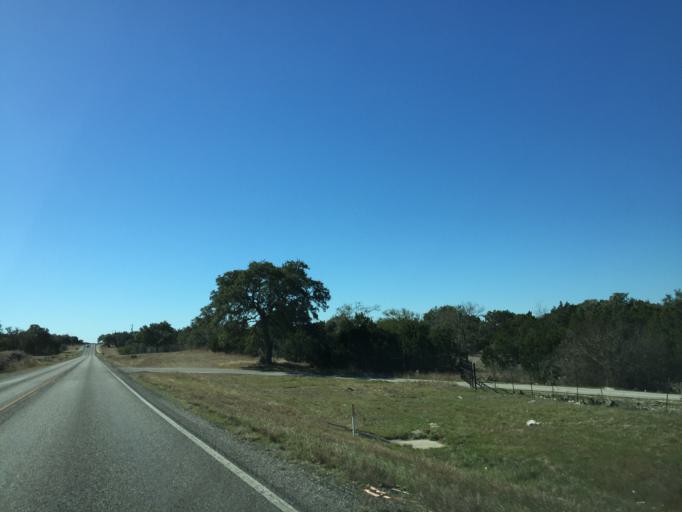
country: US
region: Texas
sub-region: Comal County
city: Garden Ridge
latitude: 29.7330
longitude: -98.3069
